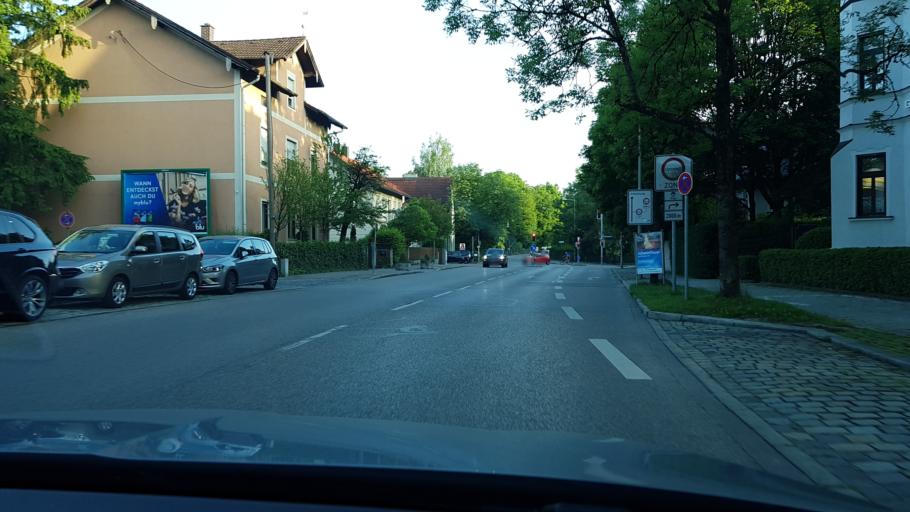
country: DE
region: Bavaria
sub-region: Upper Bavaria
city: Bogenhausen
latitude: 48.1682
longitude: 11.6243
